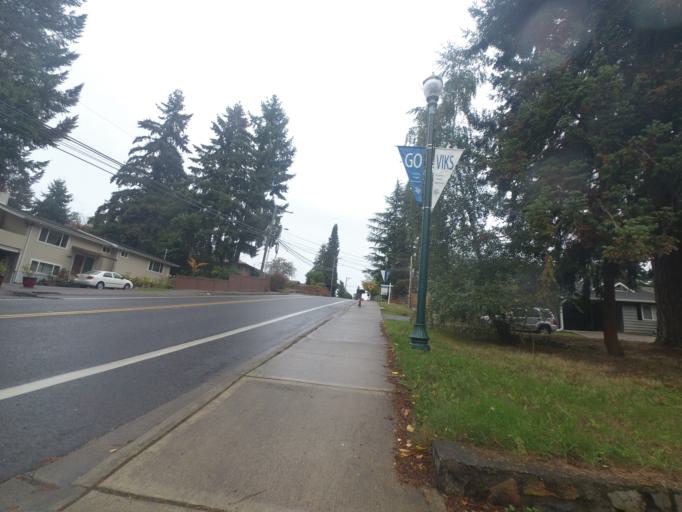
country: US
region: Washington
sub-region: Pierce County
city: University Place
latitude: 47.2207
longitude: -122.5468
